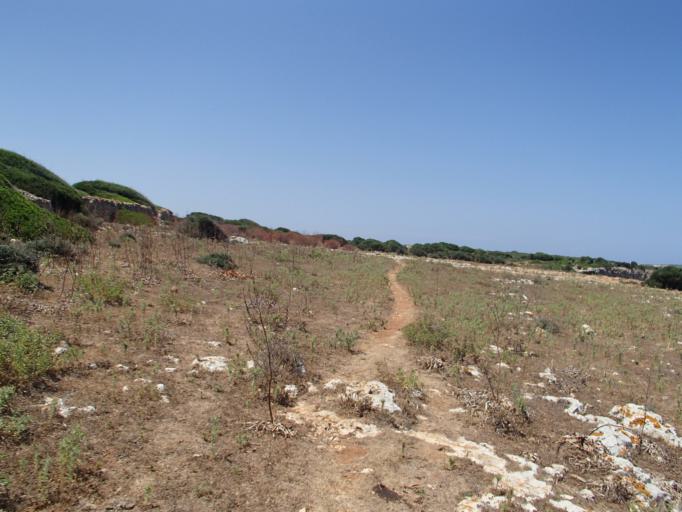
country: ES
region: Balearic Islands
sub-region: Illes Balears
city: Es Castell
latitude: 39.8436
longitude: 4.3024
